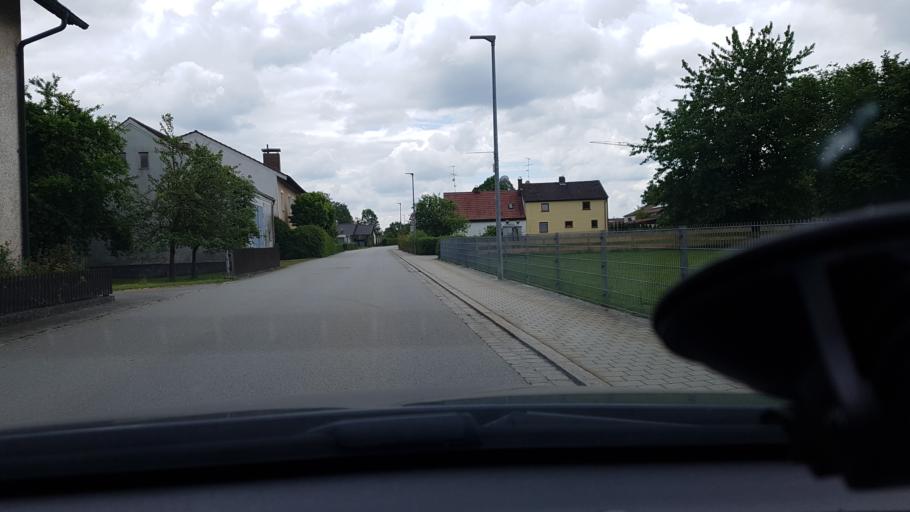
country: AT
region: Upper Austria
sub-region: Politischer Bezirk Scharding
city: Sankt Marienkirchen bei Schaerding
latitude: 48.4022
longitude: 13.3904
